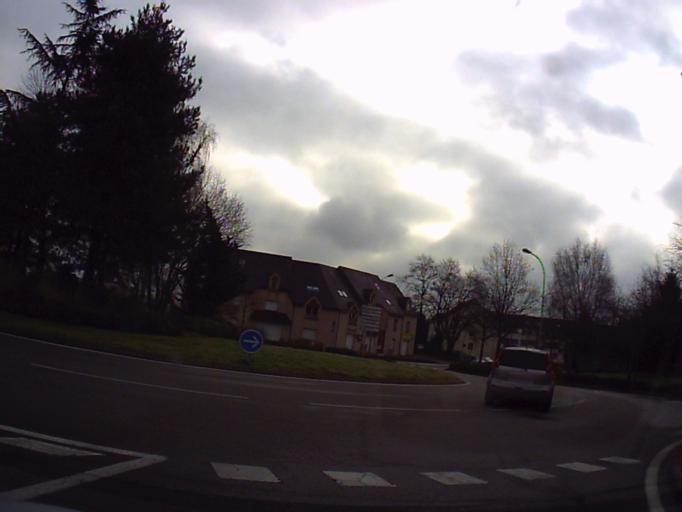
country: FR
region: Brittany
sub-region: Departement du Morbihan
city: Vannes
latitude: 47.6413
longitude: -2.7715
